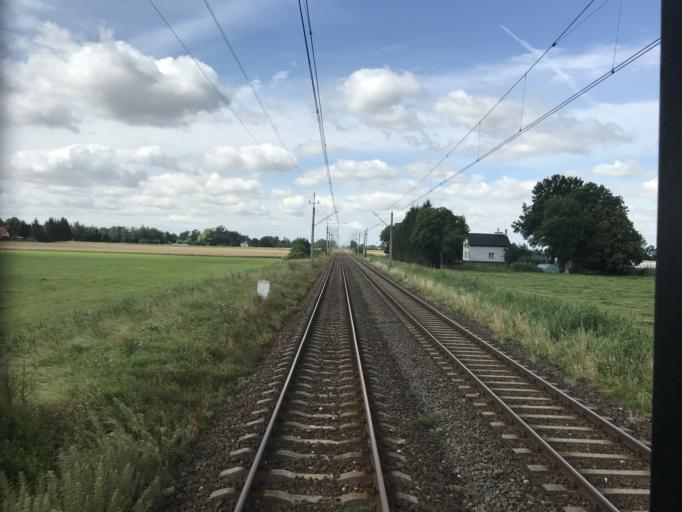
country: PL
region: Warmian-Masurian Voivodeship
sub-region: Powiat elblaski
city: Gronowo Elblaskie
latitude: 54.0857
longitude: 19.2952
